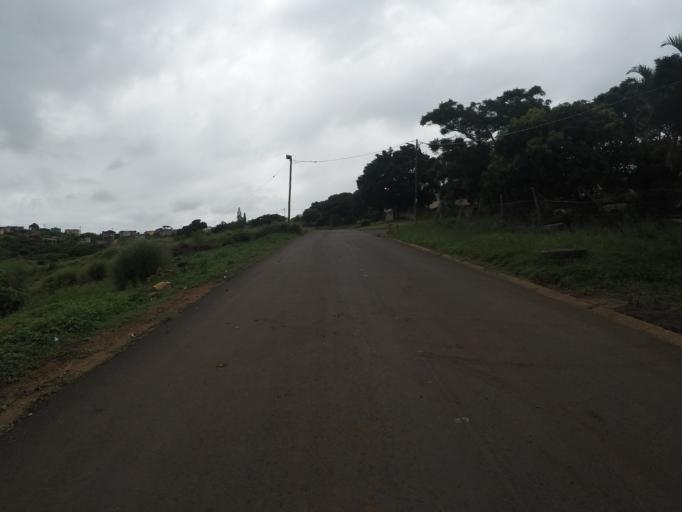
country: ZA
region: KwaZulu-Natal
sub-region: uThungulu District Municipality
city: Empangeni
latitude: -28.7719
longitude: 31.8611
